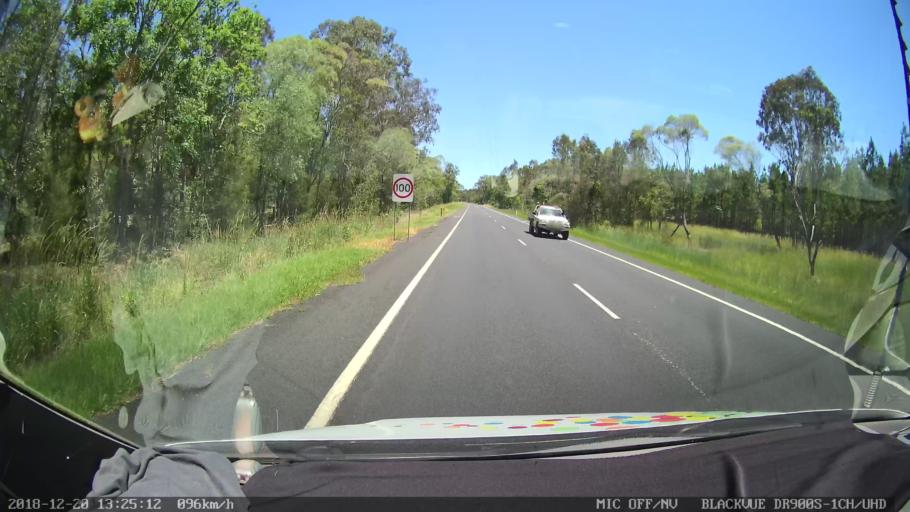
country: AU
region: New South Wales
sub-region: Richmond Valley
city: Casino
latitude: -29.1279
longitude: 152.9972
